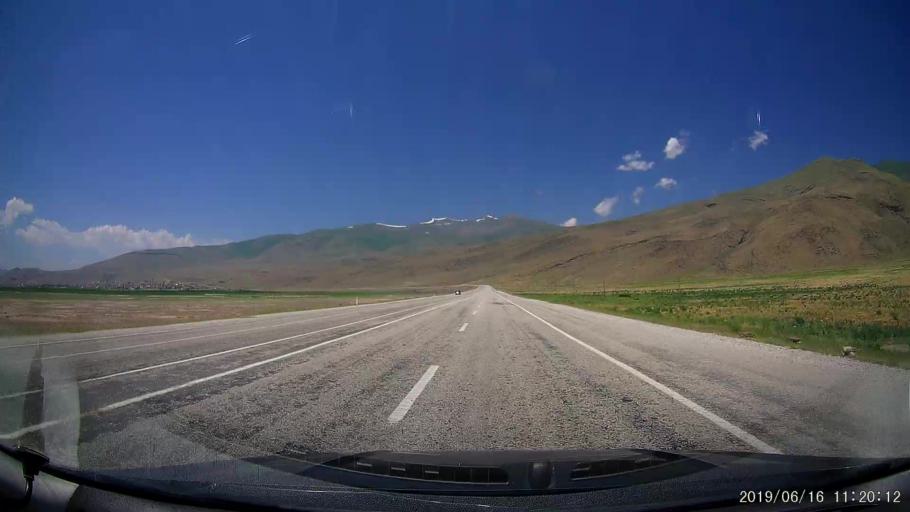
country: TR
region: Agri
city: Dogubayazit
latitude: 39.6978
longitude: 44.0961
